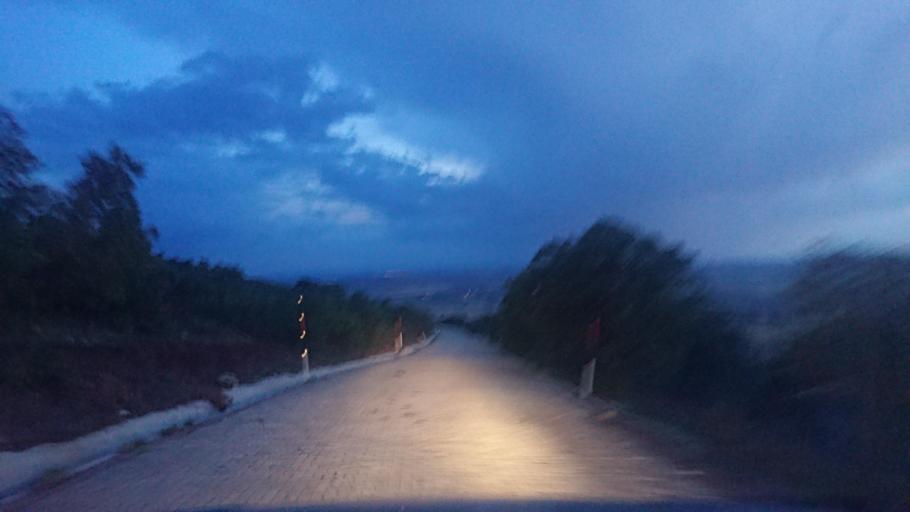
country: TR
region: Aksaray
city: Ortakoy
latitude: 38.6422
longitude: 34.0208
